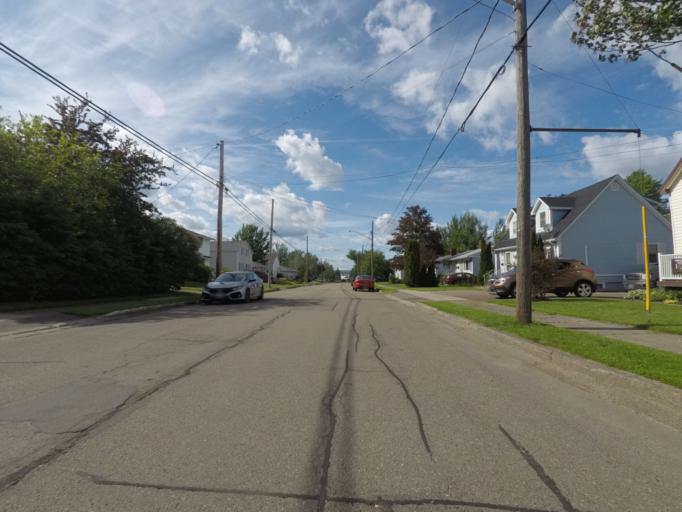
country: CA
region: New Brunswick
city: Moncton
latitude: 46.1017
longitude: -64.8215
